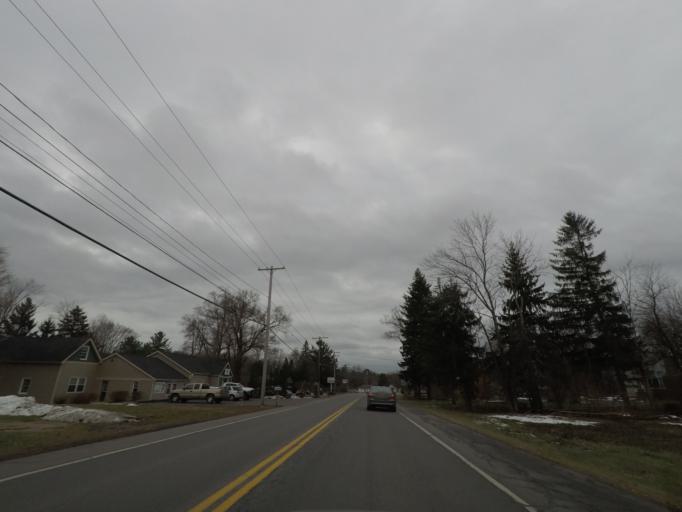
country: US
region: New York
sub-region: Schenectady County
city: East Glenville
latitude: 42.9017
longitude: -73.9055
